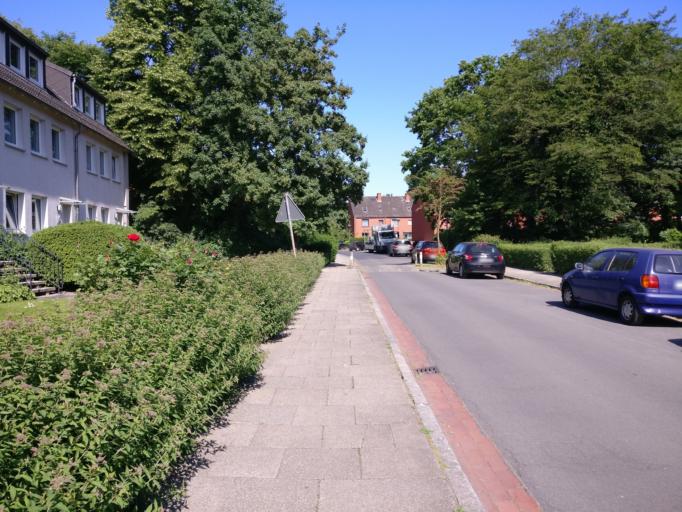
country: DE
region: Lower Saxony
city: Lilienthal
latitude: 53.1054
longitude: 8.8721
